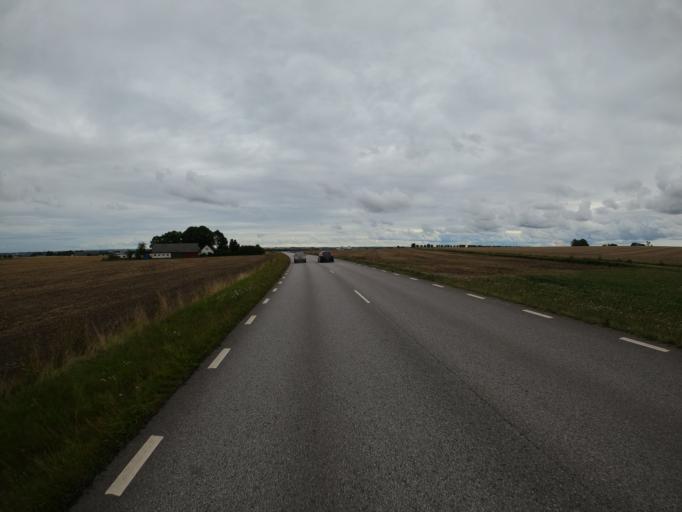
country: SE
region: Skane
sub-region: Lunds Kommun
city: Lund
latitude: 55.7559
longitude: 13.2210
